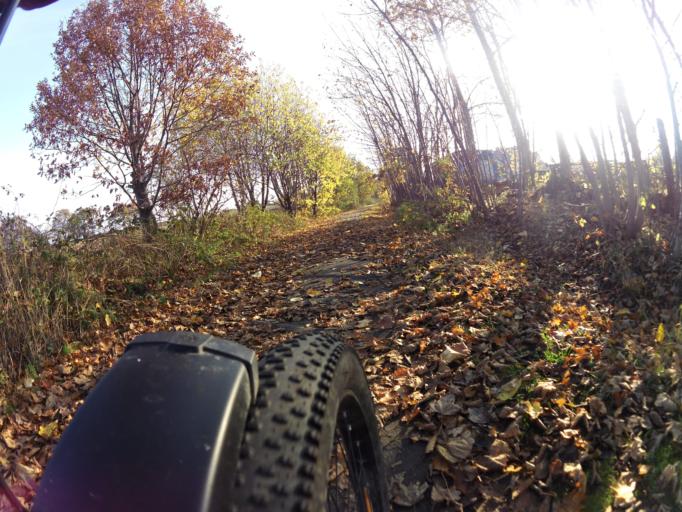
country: PL
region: Pomeranian Voivodeship
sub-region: Powiat pucki
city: Krokowa
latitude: 54.7833
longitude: 18.1727
